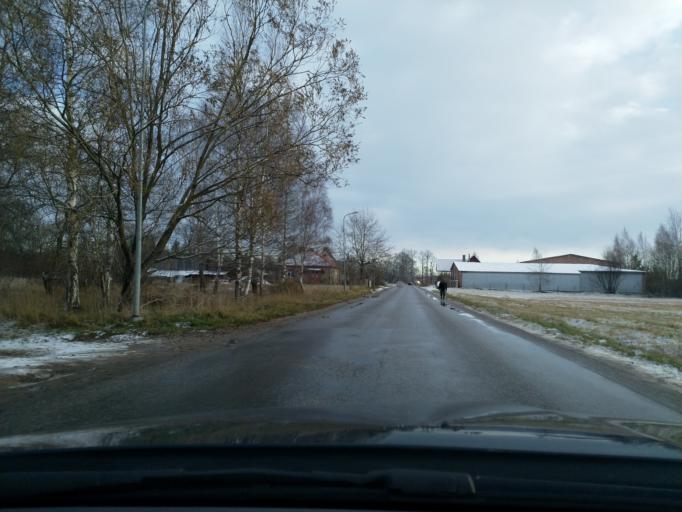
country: LV
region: Kuldigas Rajons
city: Kuldiga
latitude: 56.9601
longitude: 21.9886
